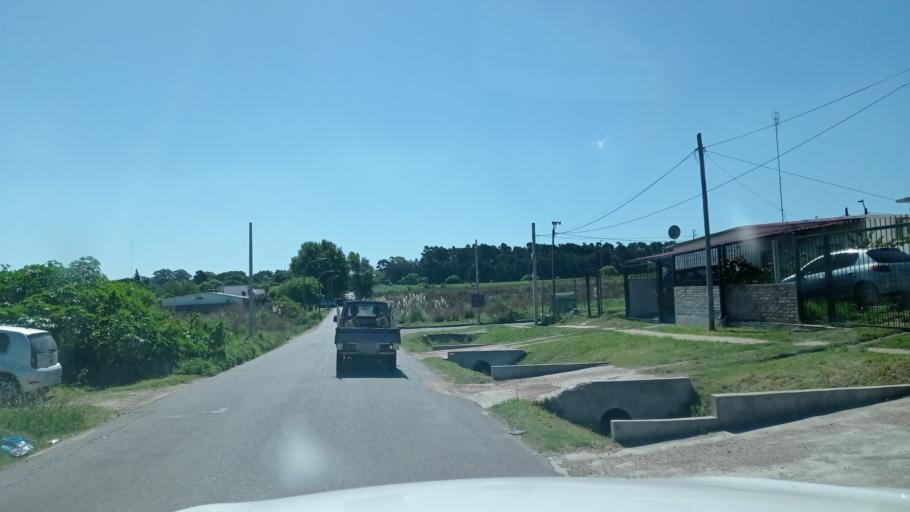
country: UY
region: Canelones
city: La Paz
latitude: -34.8300
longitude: -56.2360
